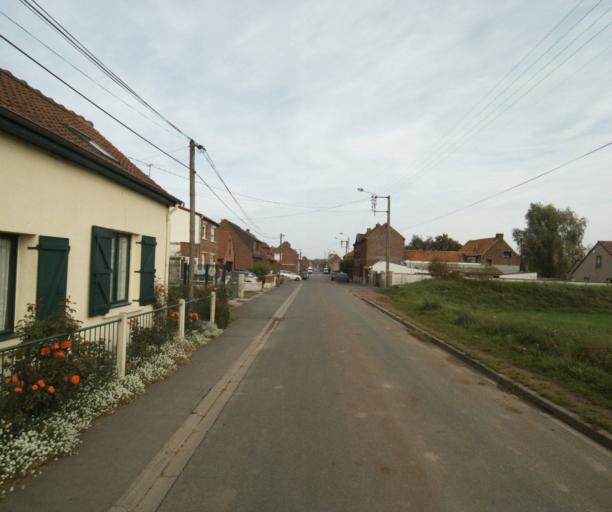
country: FR
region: Nord-Pas-de-Calais
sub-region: Departement du Nord
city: Sainghin-en-Weppes
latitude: 50.5527
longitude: 2.9041
